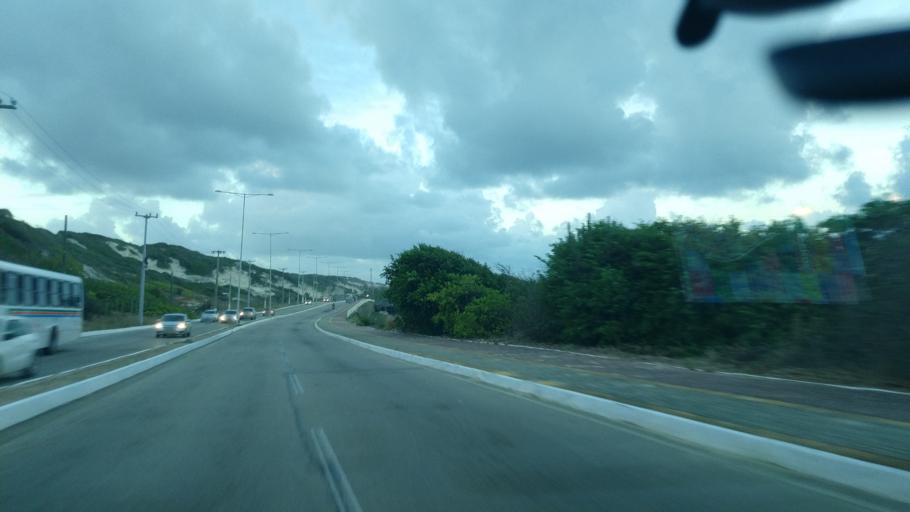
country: BR
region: Rio Grande do Norte
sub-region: Natal
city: Natal
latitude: -5.8388
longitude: -35.1822
